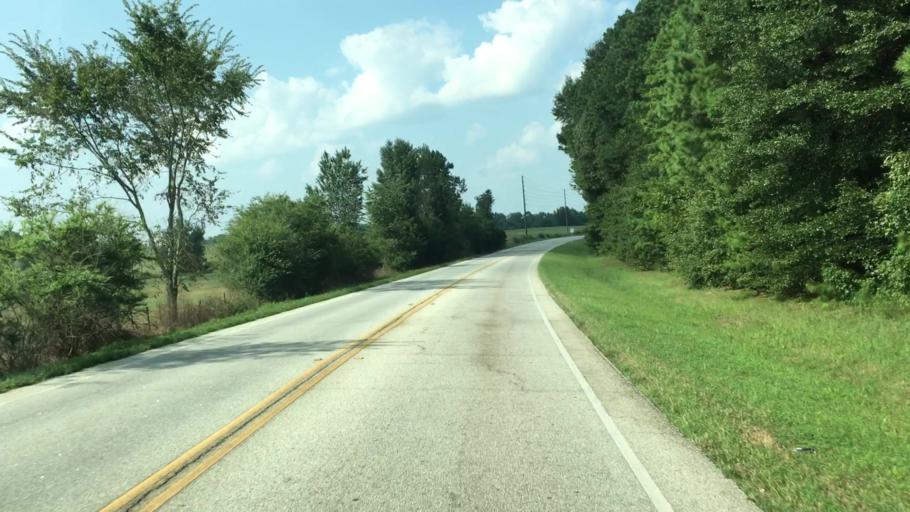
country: US
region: Georgia
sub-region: Newton County
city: Covington
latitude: 33.4683
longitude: -83.7535
